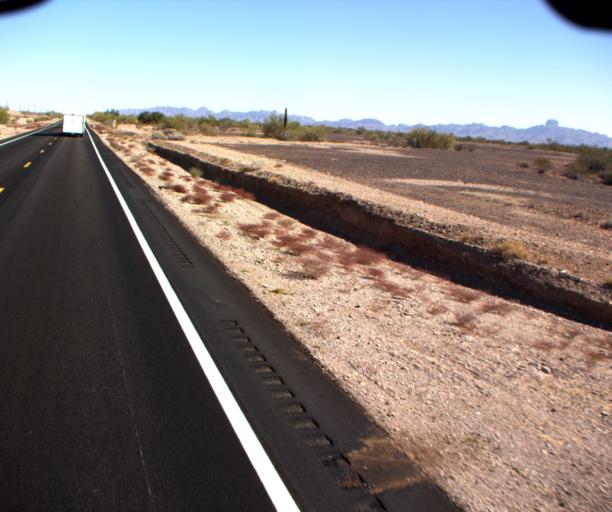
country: US
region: Arizona
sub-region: Yuma County
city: Wellton
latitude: 32.9824
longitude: -114.2888
